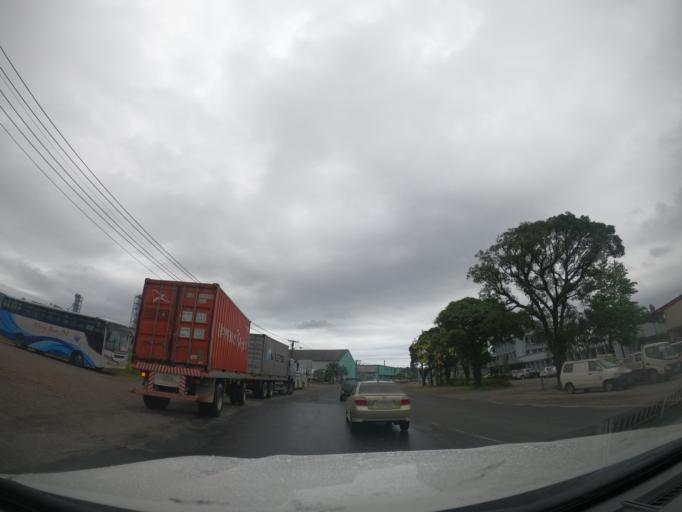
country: FJ
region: Central
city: Suva
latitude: -18.1254
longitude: 178.4315
